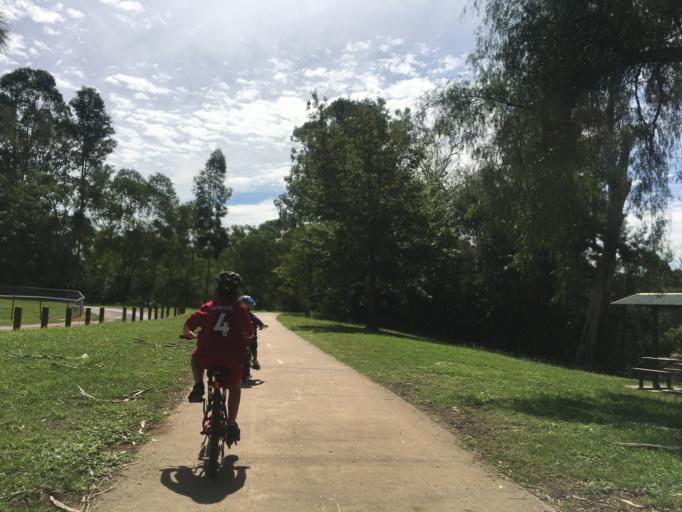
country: AU
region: New South Wales
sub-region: Camden
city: Camden South
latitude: -34.0688
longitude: 150.6992
